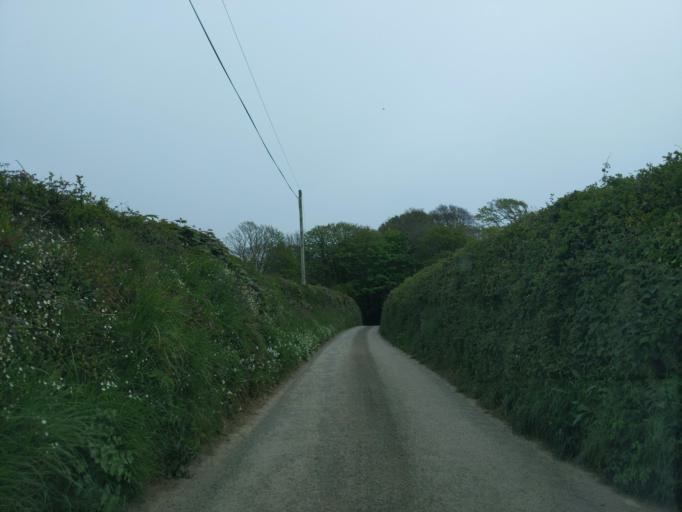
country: GB
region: England
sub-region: Cornwall
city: St Austell
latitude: 50.3089
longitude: -4.7651
